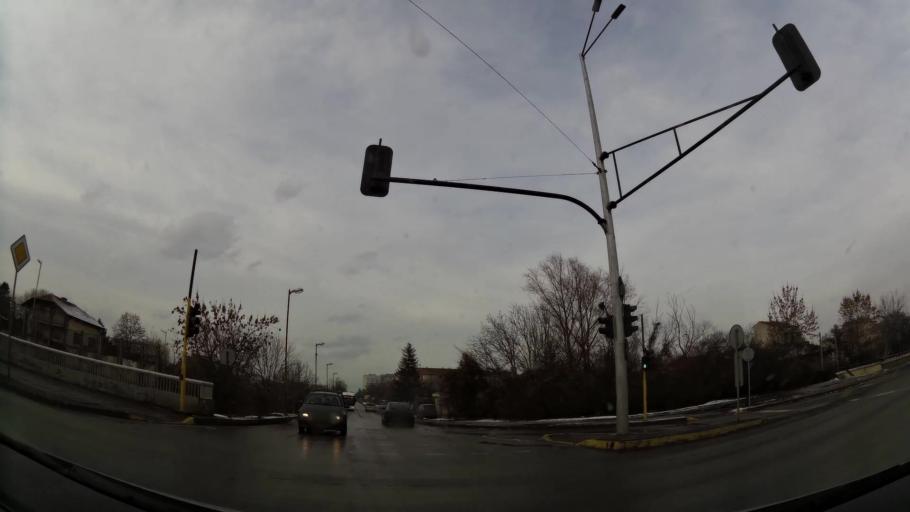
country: BG
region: Sofia-Capital
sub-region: Stolichna Obshtina
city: Sofia
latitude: 42.7014
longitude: 23.3779
